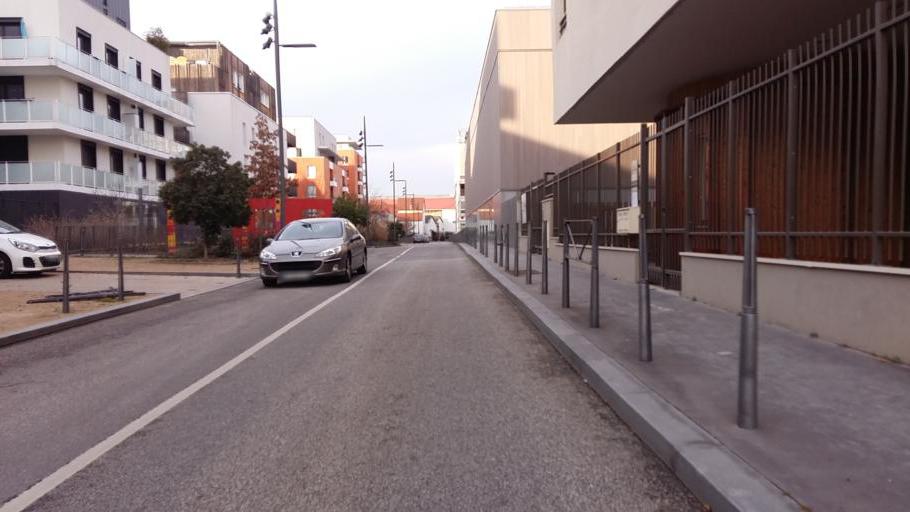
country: FR
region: Rhone-Alpes
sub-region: Departement du Rhone
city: Lyon
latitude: 45.7358
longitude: 4.8325
